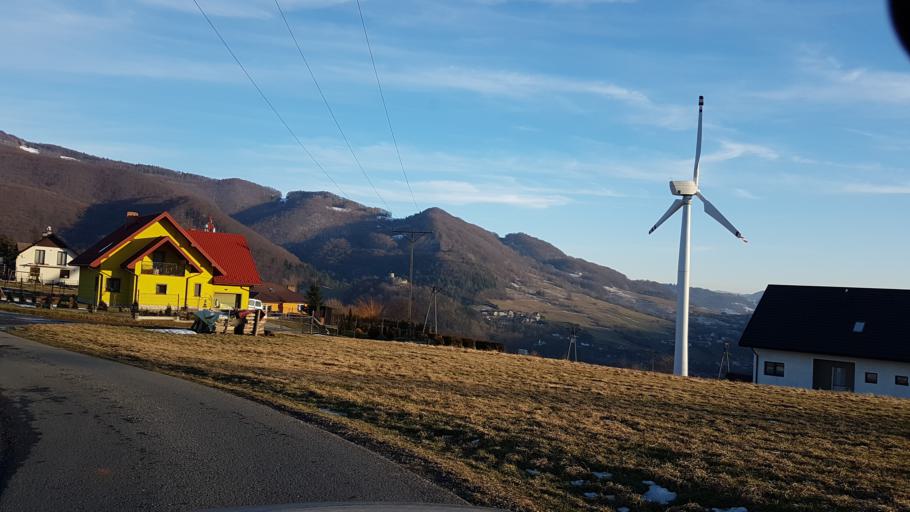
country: PL
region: Lesser Poland Voivodeship
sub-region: Powiat nowosadecki
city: Rytro
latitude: 49.4940
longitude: 20.6716
